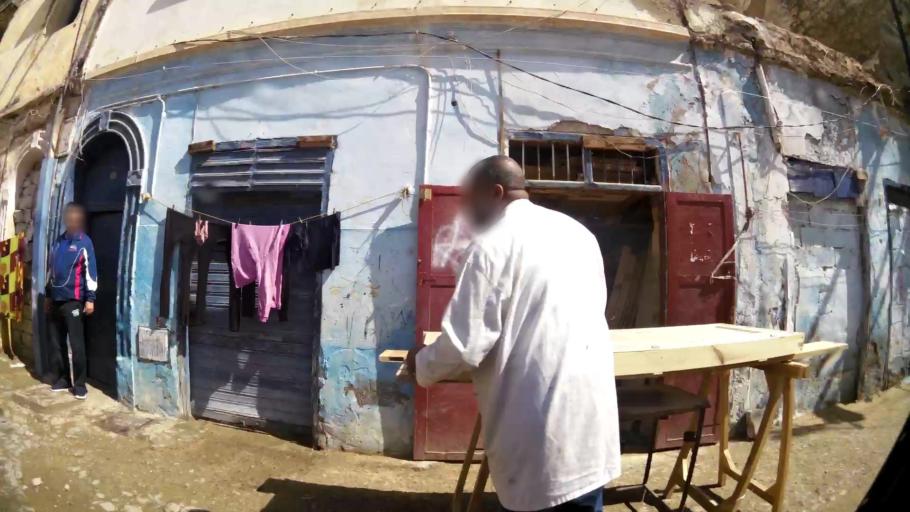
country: MA
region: Grand Casablanca
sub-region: Casablanca
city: Casablanca
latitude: 33.6024
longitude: -7.6278
